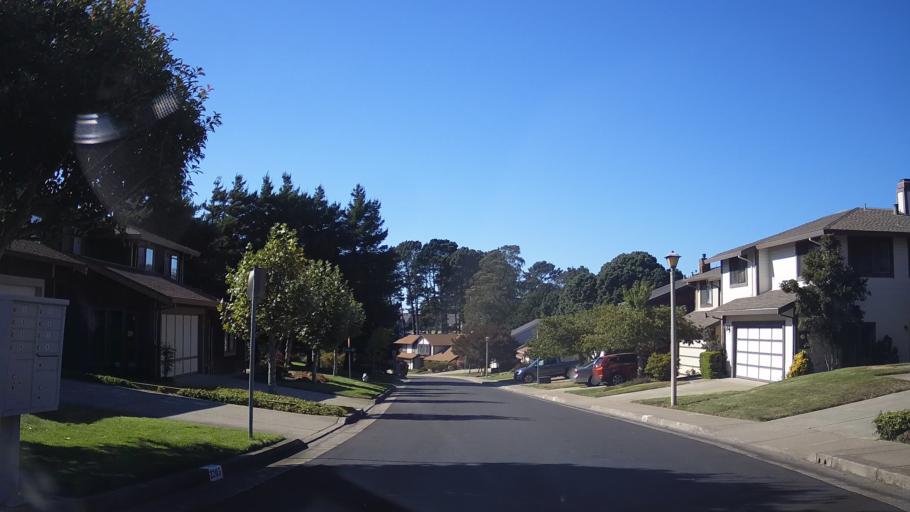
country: US
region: California
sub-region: Contra Costa County
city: East Richmond Heights
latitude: 37.9322
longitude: -122.3000
